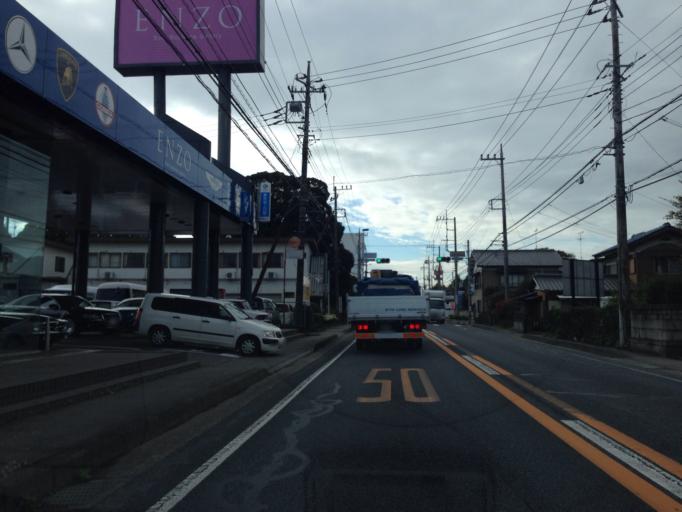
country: JP
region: Ibaraki
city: Ushiku
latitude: 35.9932
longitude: 140.1473
